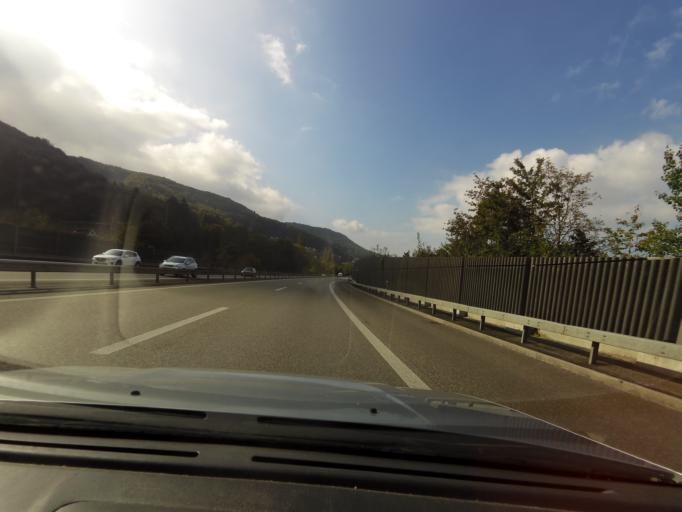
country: CH
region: Aargau
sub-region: Bezirk Rheinfelden
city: Stein
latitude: 47.5409
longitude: 7.9565
